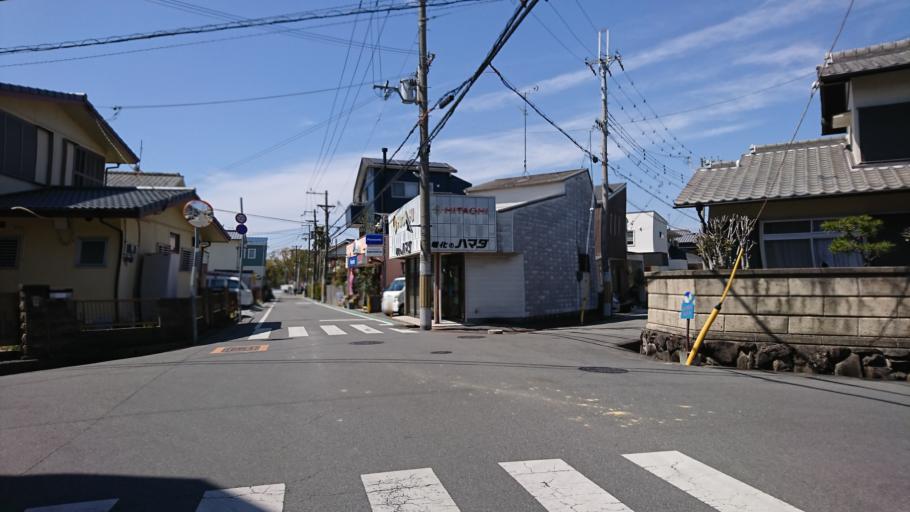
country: JP
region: Hyogo
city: Kakogawacho-honmachi
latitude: 34.7477
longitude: 134.8751
